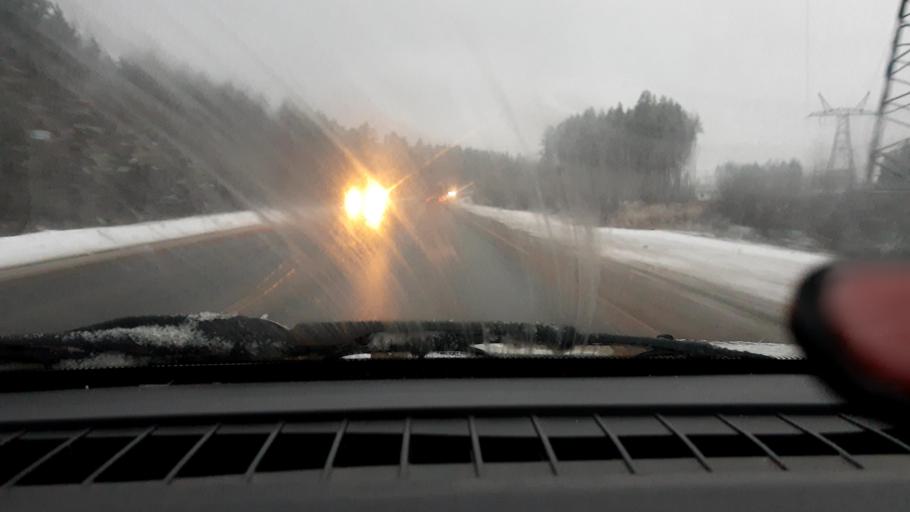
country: RU
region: Nizjnij Novgorod
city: Kstovo
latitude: 56.1680
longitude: 44.1545
